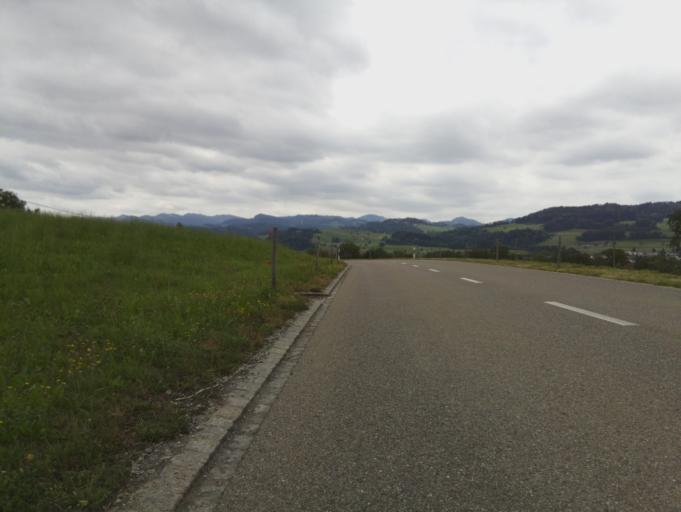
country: CH
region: Saint Gallen
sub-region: Wahlkreis Wil
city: Jonschwil
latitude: 47.4142
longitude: 9.0824
